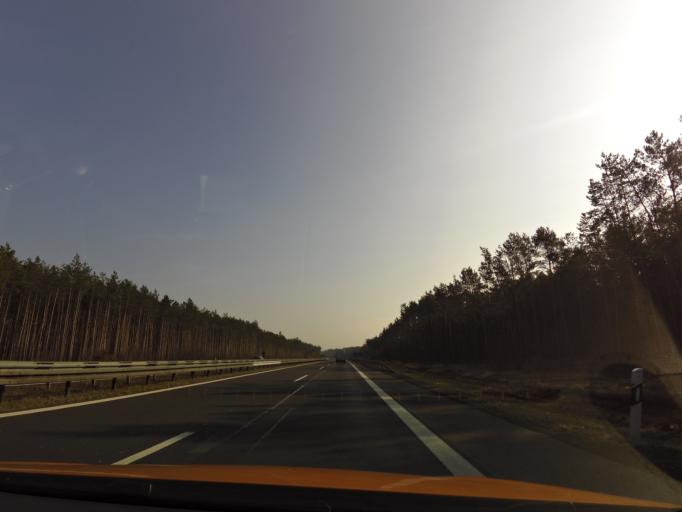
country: DE
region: Brandenburg
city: Spreenhagen
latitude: 52.3148
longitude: 13.9121
